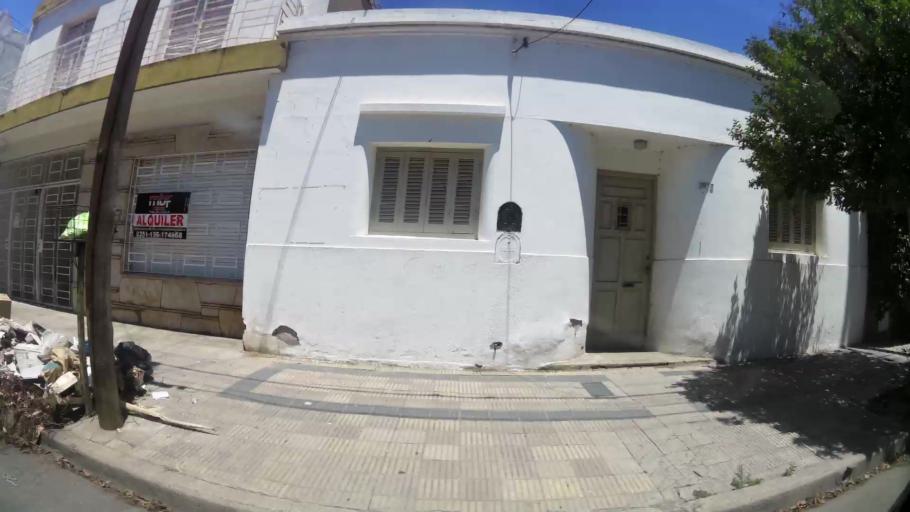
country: AR
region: Cordoba
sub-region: Departamento de Capital
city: Cordoba
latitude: -31.4014
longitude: -64.2198
